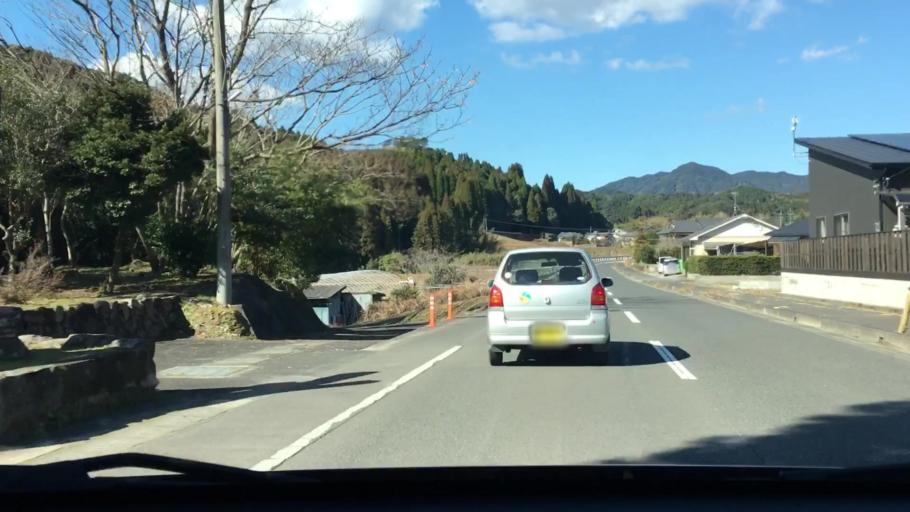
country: JP
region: Kagoshima
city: Ijuin
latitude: 31.6925
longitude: 130.4633
